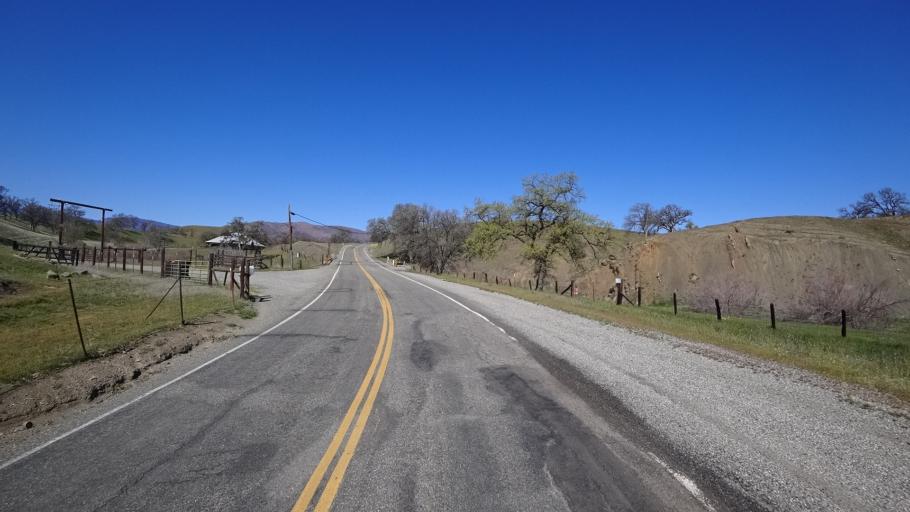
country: US
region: California
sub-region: Glenn County
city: Orland
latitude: 39.6825
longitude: -122.5355
